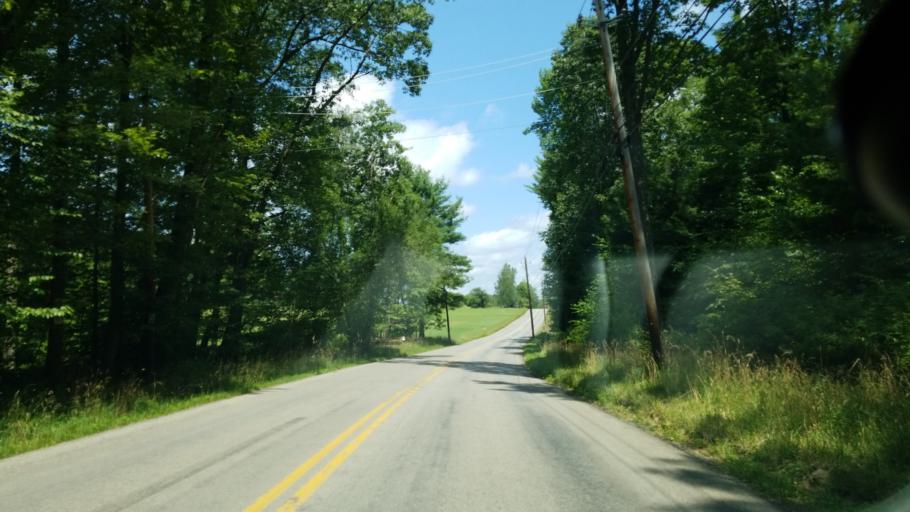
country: US
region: Pennsylvania
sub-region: Jefferson County
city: Brookville
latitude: 41.2907
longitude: -79.0948
